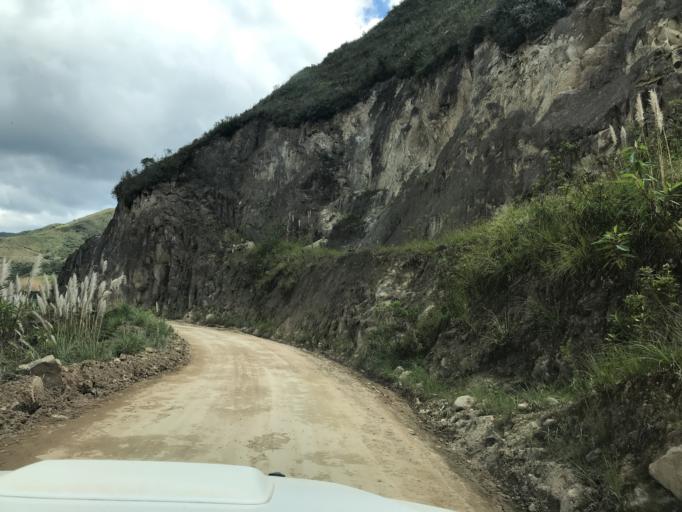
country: PE
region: Cajamarca
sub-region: Provincia de Chota
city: Querocoto
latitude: -6.3699
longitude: -79.0371
